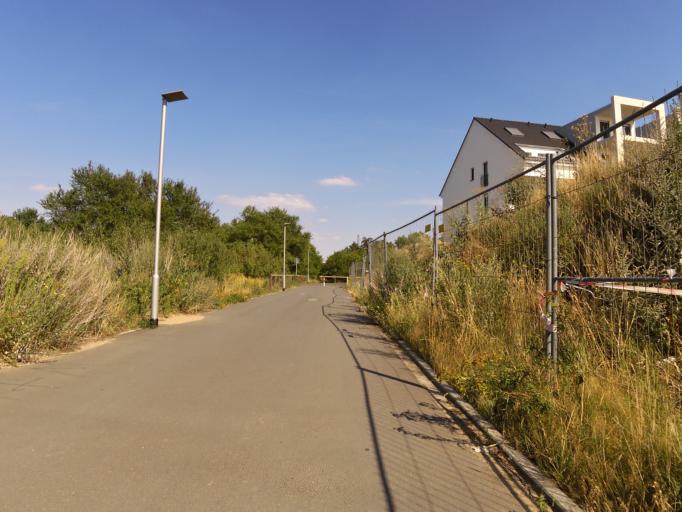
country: DE
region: Hesse
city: Morfelden-Walldorf
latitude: 49.9822
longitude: 8.5653
